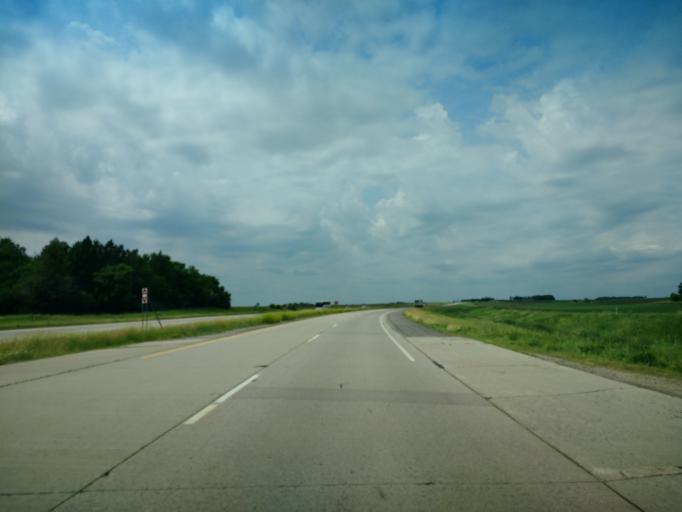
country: US
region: Minnesota
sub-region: Cottonwood County
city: Mountain Lake
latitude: 43.9499
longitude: -94.7991
